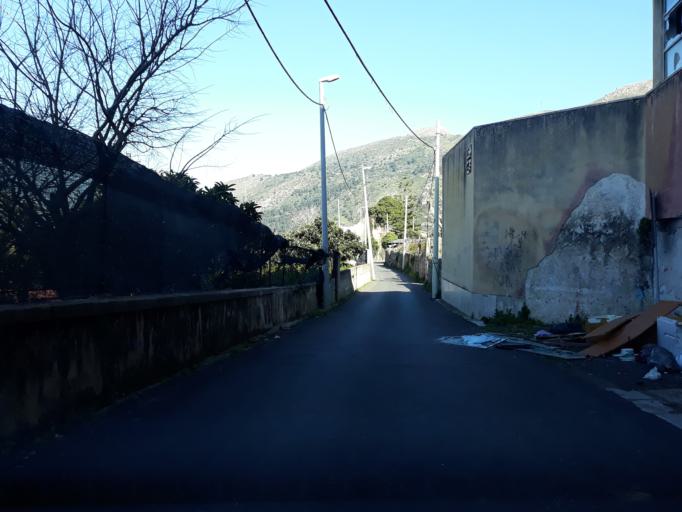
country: IT
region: Sicily
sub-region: Palermo
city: Villa Ciambra
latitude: 38.0754
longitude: 13.3584
